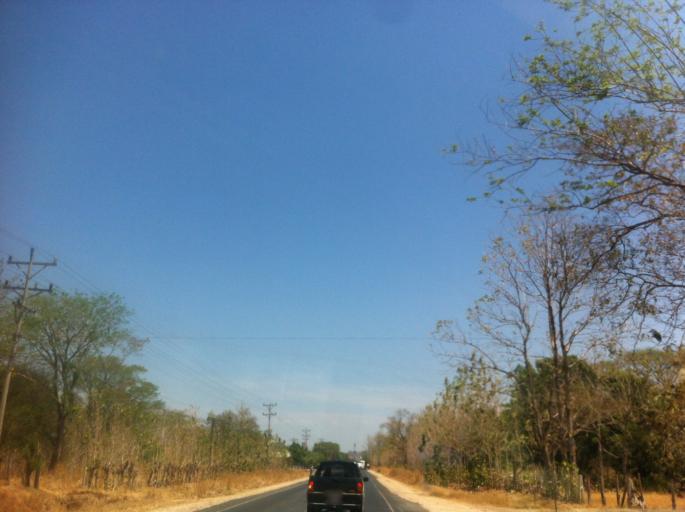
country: CR
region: Guanacaste
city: Santa Cruz
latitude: 10.2979
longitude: -85.5875
